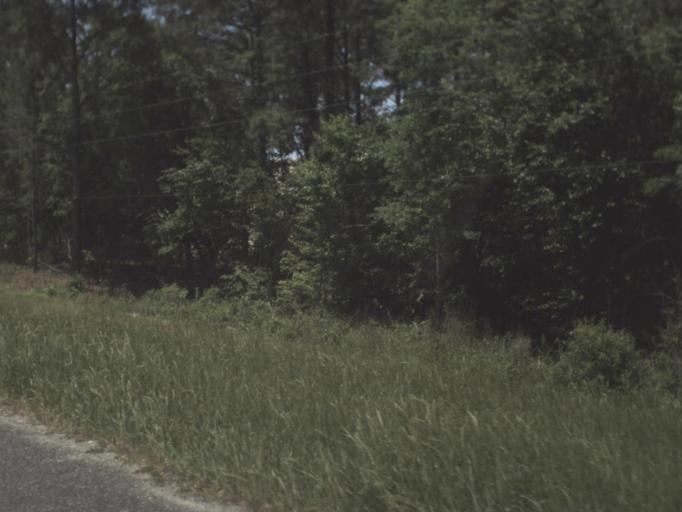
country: US
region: Florida
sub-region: Jefferson County
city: Monticello
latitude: 30.5063
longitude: -83.8778
